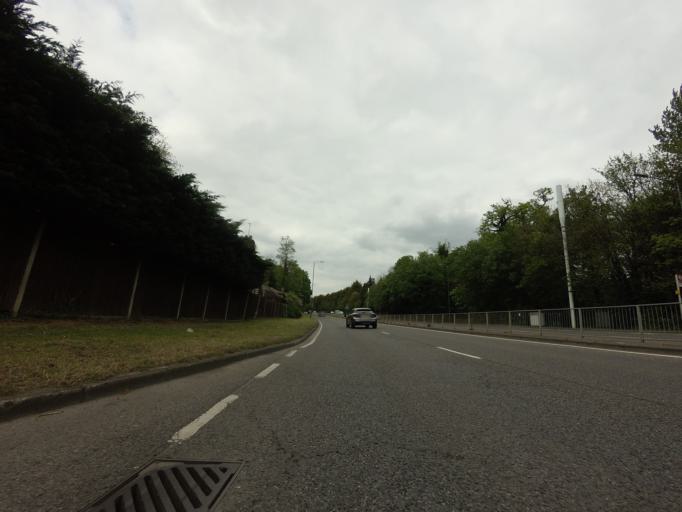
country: GB
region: England
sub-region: Greater London
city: Bexley
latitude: 51.4199
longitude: 0.1326
